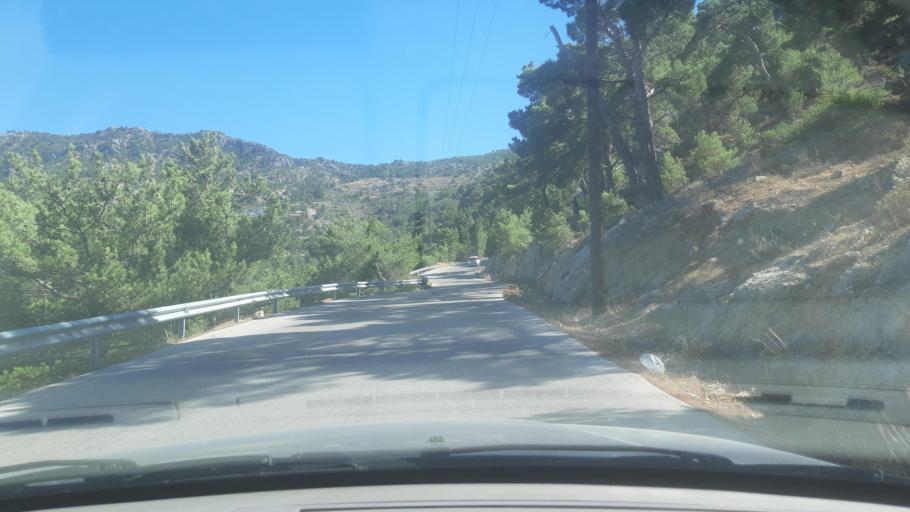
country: GR
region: South Aegean
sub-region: Nomos Dodekanisou
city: Karpathos
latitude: 35.5836
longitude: 27.1795
